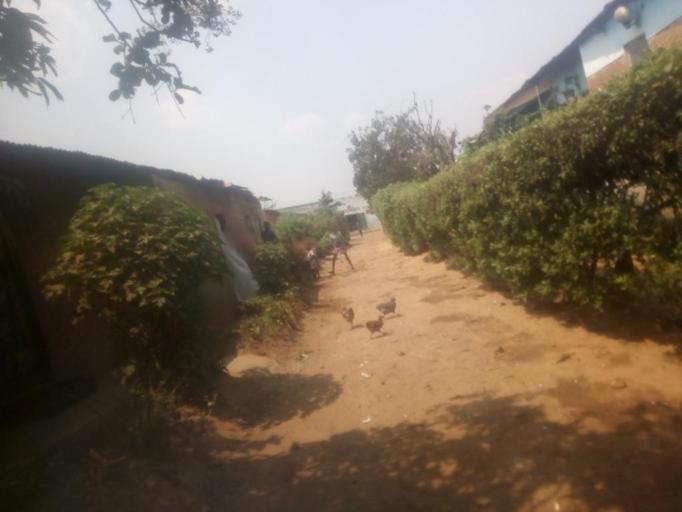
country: ZM
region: Lusaka
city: Lusaka
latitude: -15.4058
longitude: 28.3766
